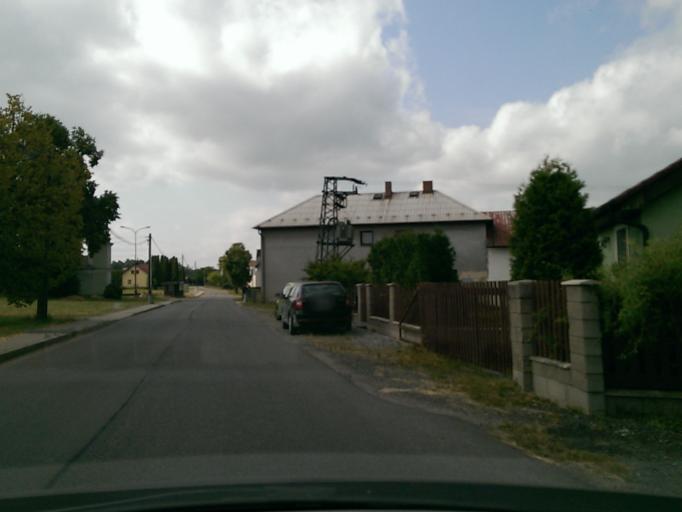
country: CZ
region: Central Bohemia
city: Bakov nad Jizerou
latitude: 50.4794
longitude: 14.8914
